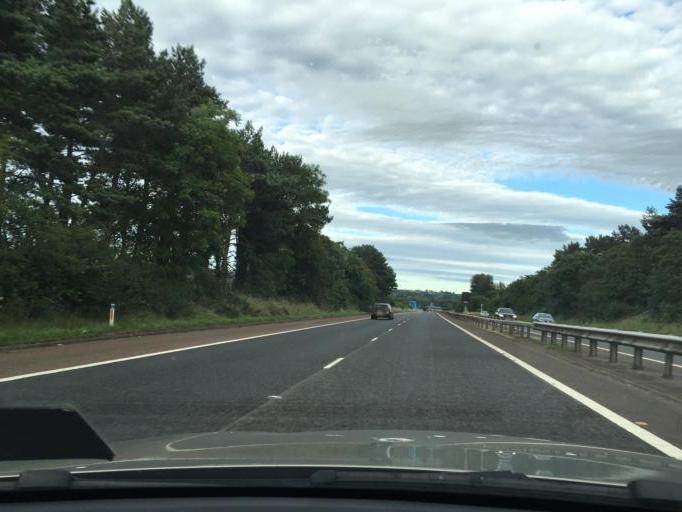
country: GB
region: Northern Ireland
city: Randalstown
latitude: 54.7444
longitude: -6.2522
